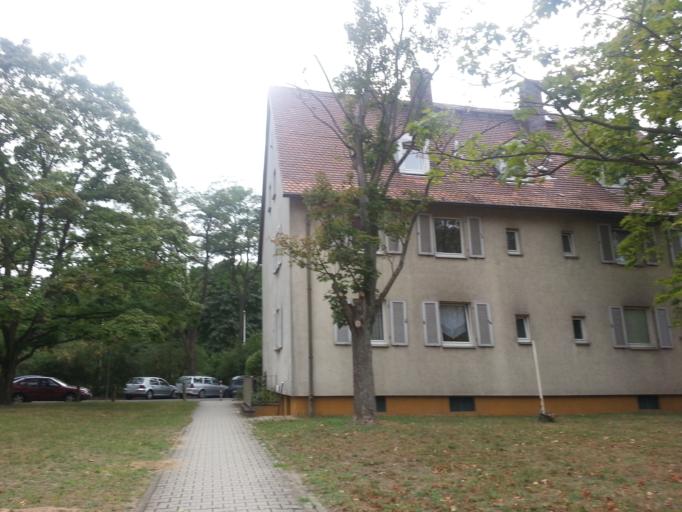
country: DE
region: Hesse
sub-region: Regierungsbezirk Darmstadt
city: Darmstadt
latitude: 49.8683
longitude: 8.6221
